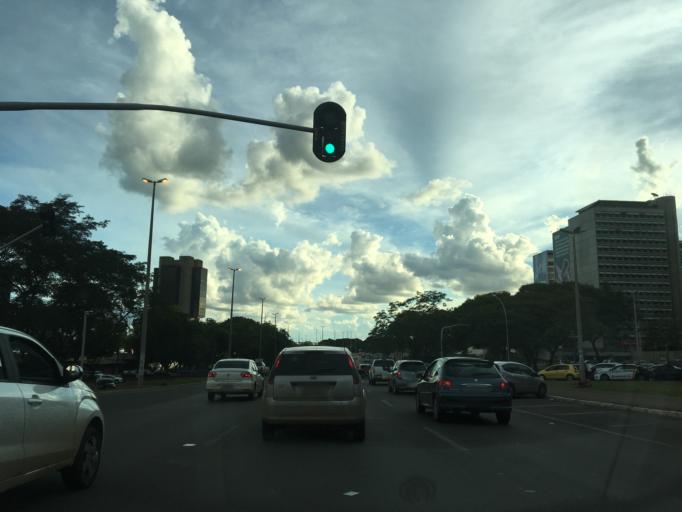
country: BR
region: Federal District
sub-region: Brasilia
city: Brasilia
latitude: -15.7973
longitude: -47.8846
